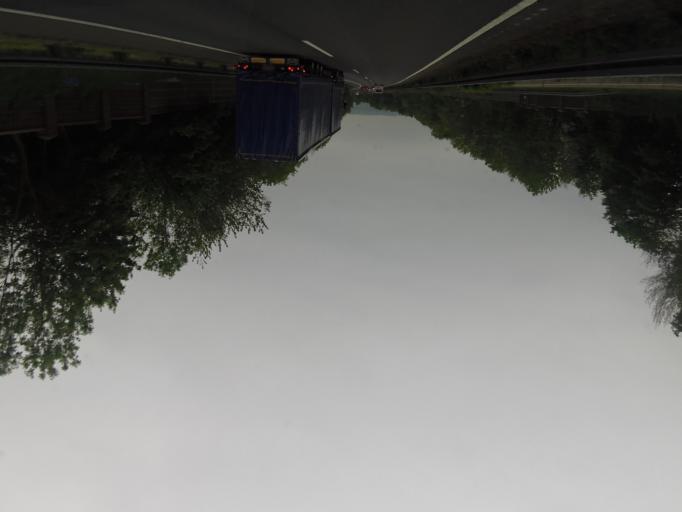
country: DE
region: Lower Saxony
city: Kalefeld
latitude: 51.8202
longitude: 10.1089
